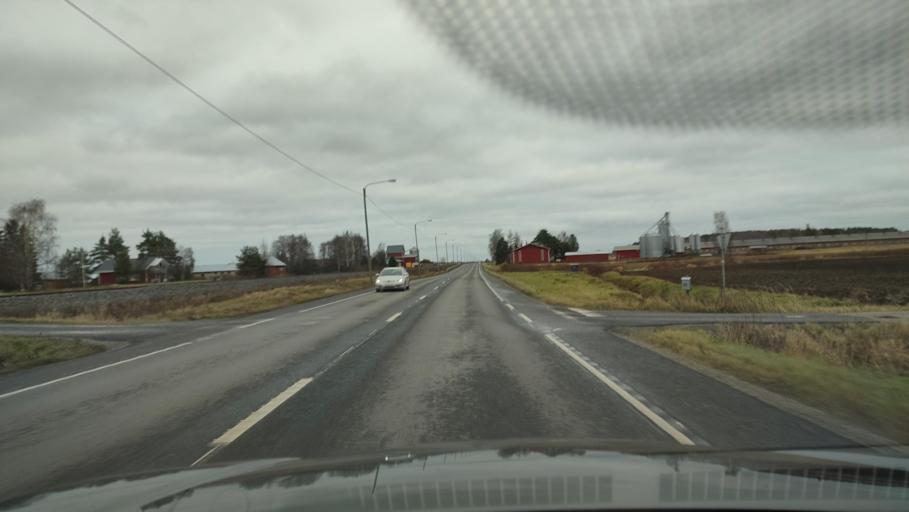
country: FI
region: Southern Ostrobothnia
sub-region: Seinaejoki
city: Ilmajoki
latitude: 62.7057
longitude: 22.5255
